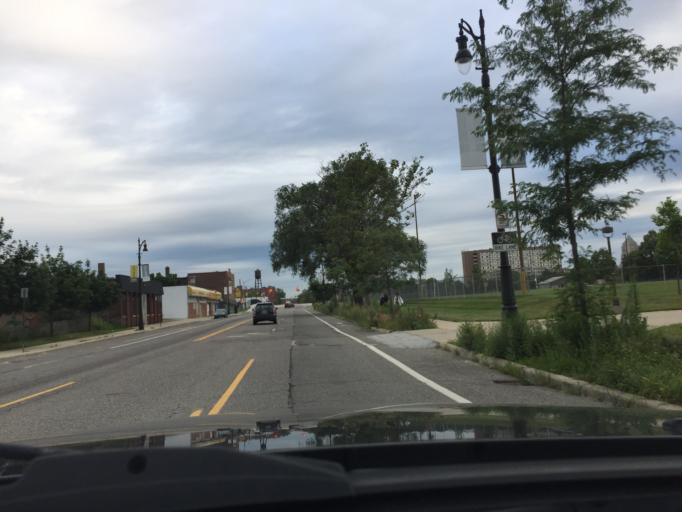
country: US
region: Michigan
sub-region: Wayne County
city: Detroit
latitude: 42.3540
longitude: -83.0798
